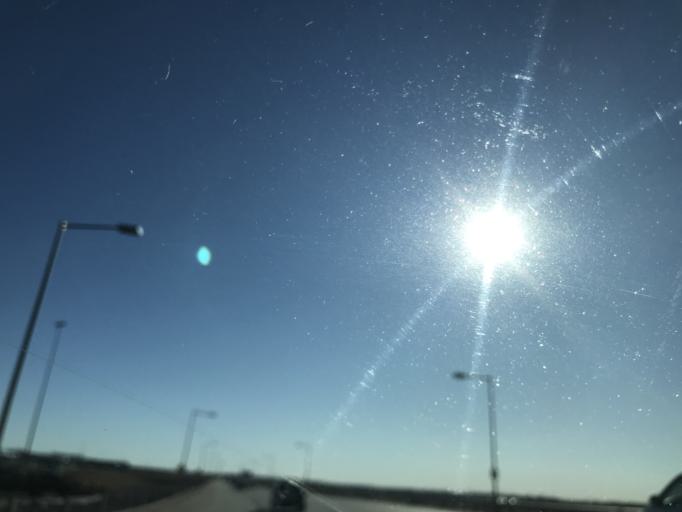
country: US
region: Colorado
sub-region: Weld County
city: Lochbuie
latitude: 39.8462
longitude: -104.6816
